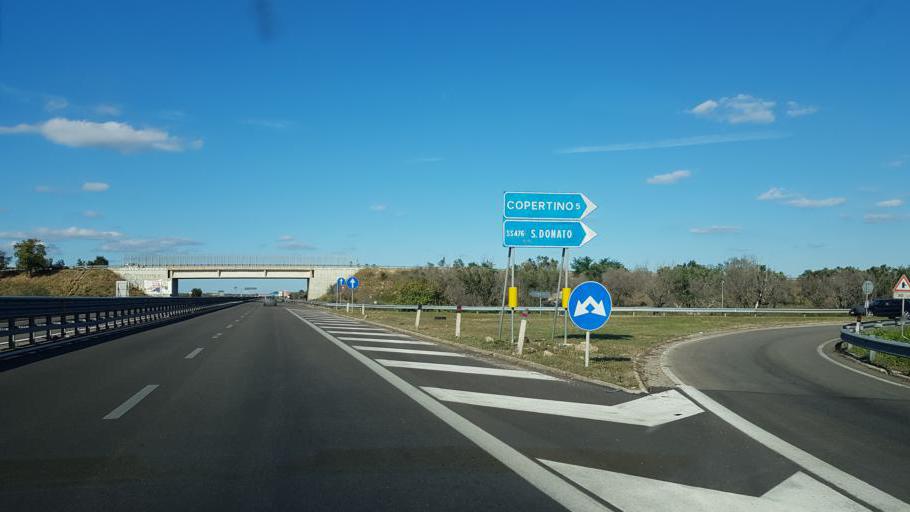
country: IT
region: Apulia
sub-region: Provincia di Lecce
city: Collemeto
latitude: 40.2564
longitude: 18.1181
